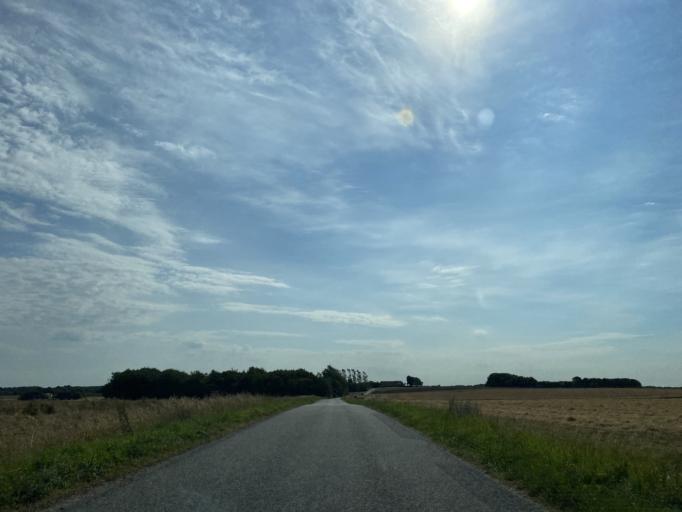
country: DK
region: Central Jutland
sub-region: Favrskov Kommune
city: Ulstrup
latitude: 56.3299
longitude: 9.7544
